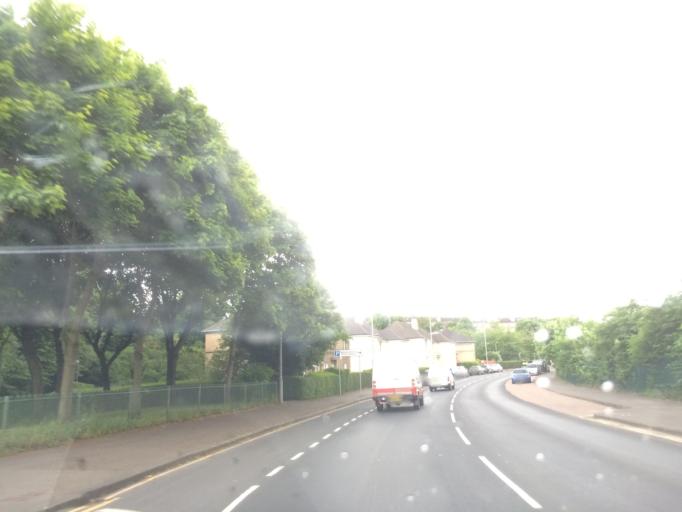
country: GB
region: Scotland
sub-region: Glasgow City
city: Glasgow
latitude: 55.8312
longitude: -4.2553
